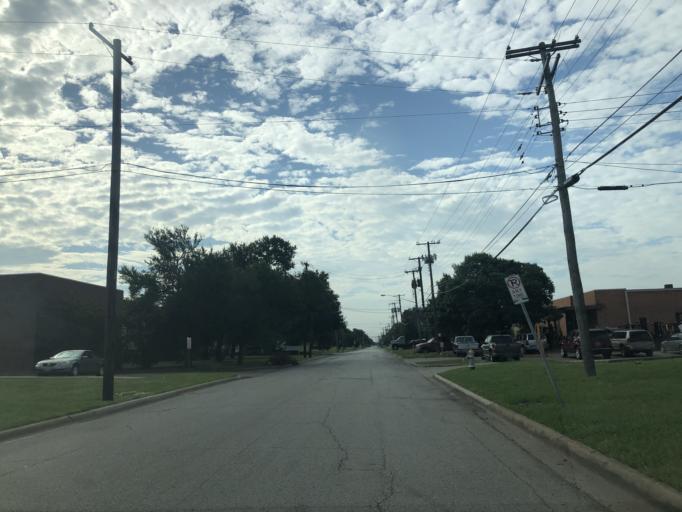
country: US
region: Texas
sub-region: Dallas County
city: Irving
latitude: 32.8213
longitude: -96.8882
